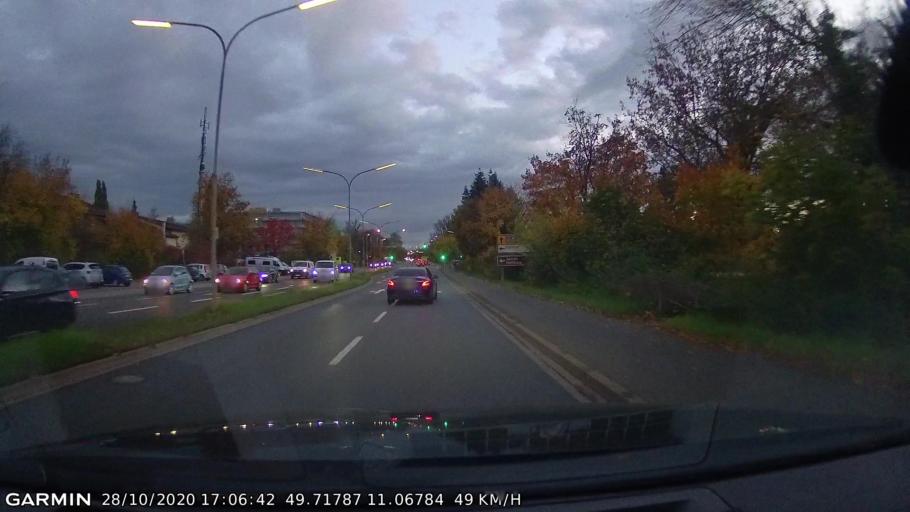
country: DE
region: Bavaria
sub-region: Upper Franconia
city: Forchheim
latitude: 49.7177
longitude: 11.0679
